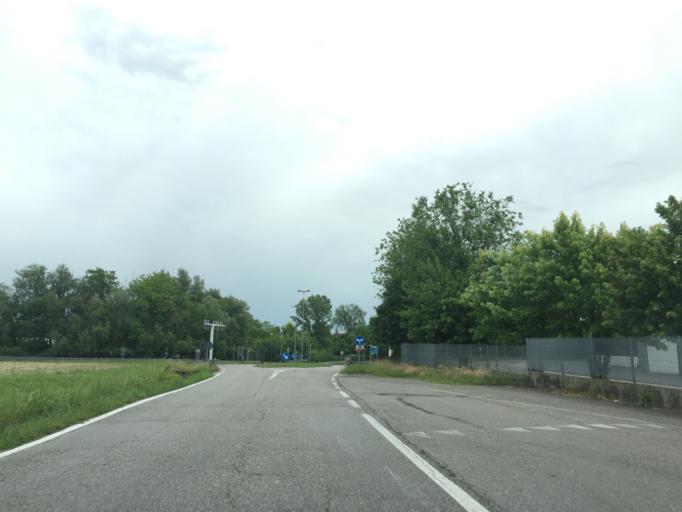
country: IT
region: Friuli Venezia Giulia
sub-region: Provincia di Pordenone
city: Porcia
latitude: 45.9580
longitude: 12.5826
